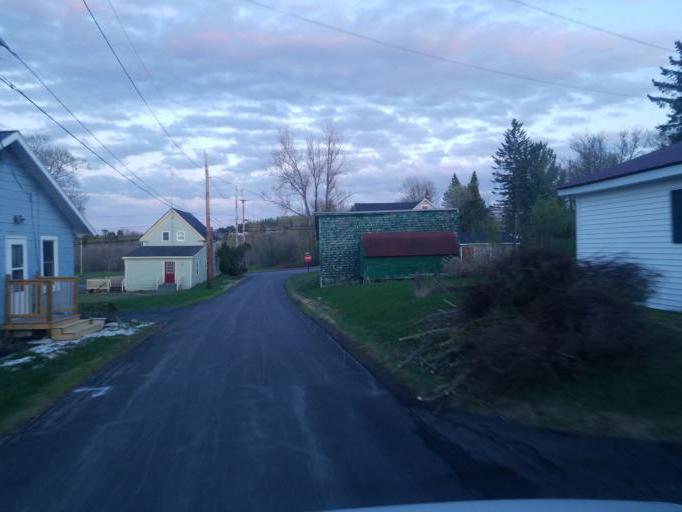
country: US
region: Maine
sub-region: Aroostook County
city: Caribou
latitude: 46.8579
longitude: -68.0230
